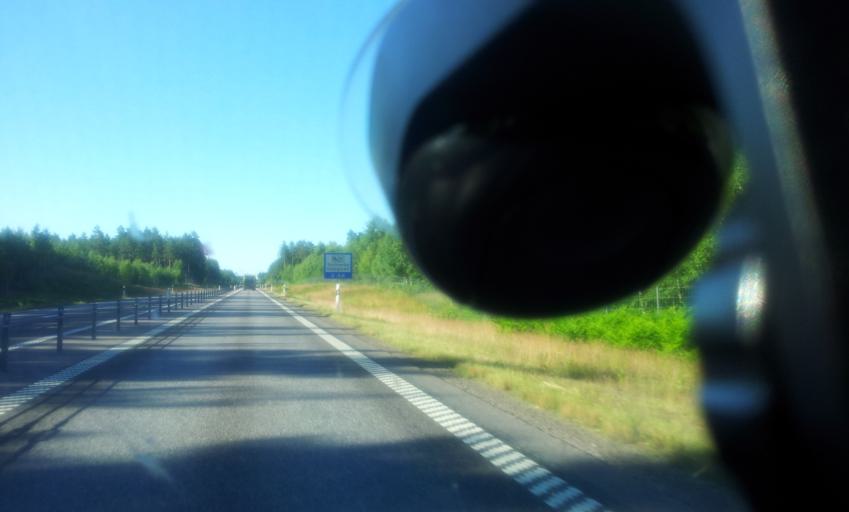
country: SE
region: Kalmar
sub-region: Kalmar Kommun
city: Ljungbyholm
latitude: 56.5265
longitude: 16.0845
